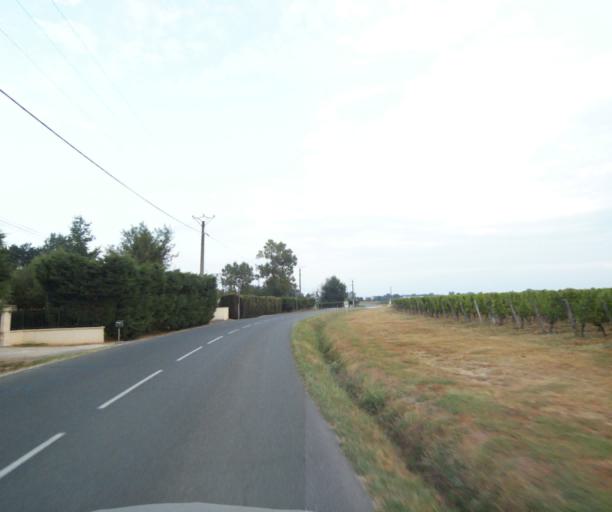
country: FR
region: Aquitaine
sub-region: Departement de la Gironde
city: Creon
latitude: 44.7653
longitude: -0.3339
